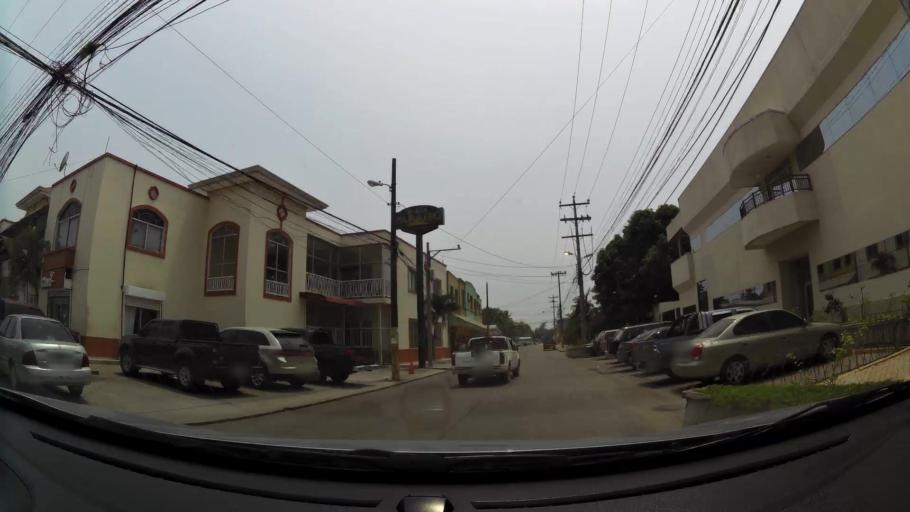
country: HN
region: Yoro
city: El Progreso
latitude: 15.4005
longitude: -87.8123
